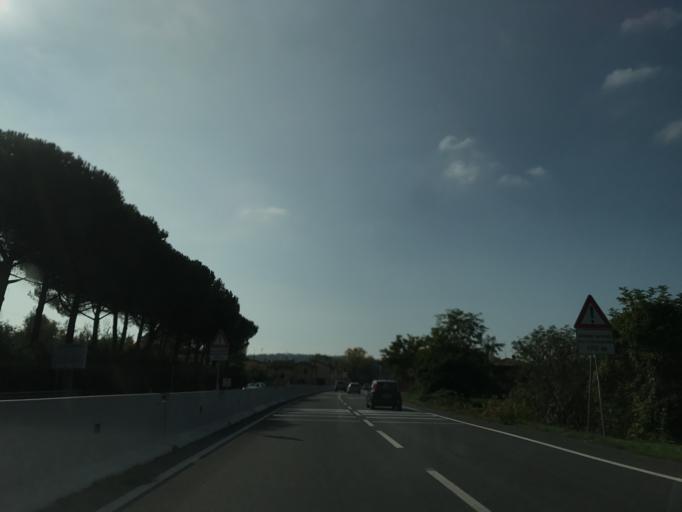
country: IT
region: Emilia-Romagna
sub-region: Provincia di Rimini
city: Cerasolo
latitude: 44.0011
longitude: 12.5426
